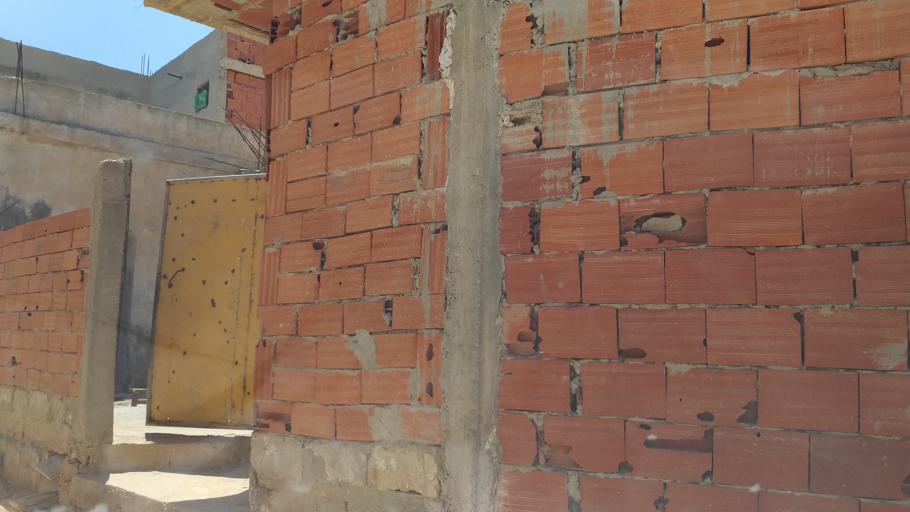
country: TN
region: Qabis
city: Gabes
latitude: 33.9420
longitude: 10.0581
